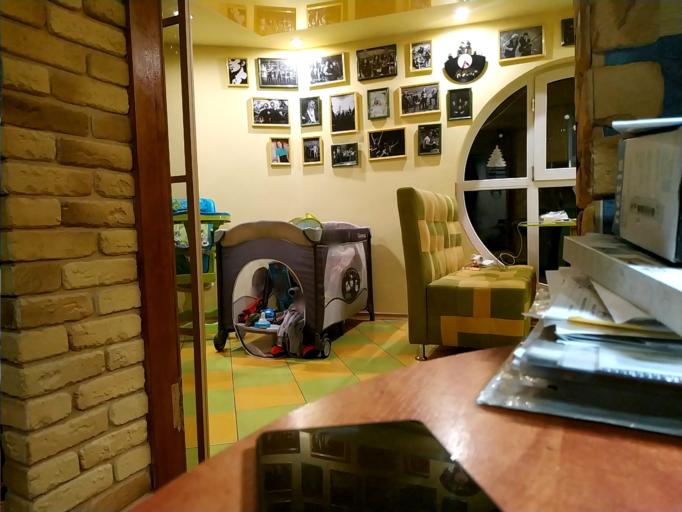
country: RU
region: Orjol
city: Naryshkino
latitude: 53.0284
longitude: 35.6865
